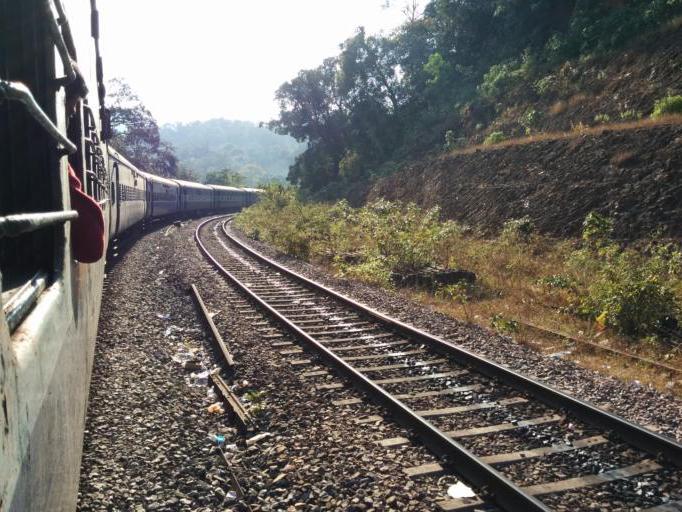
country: IN
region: Goa
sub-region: South Goa
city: Sanguem
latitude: 15.3110
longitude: 74.2954
